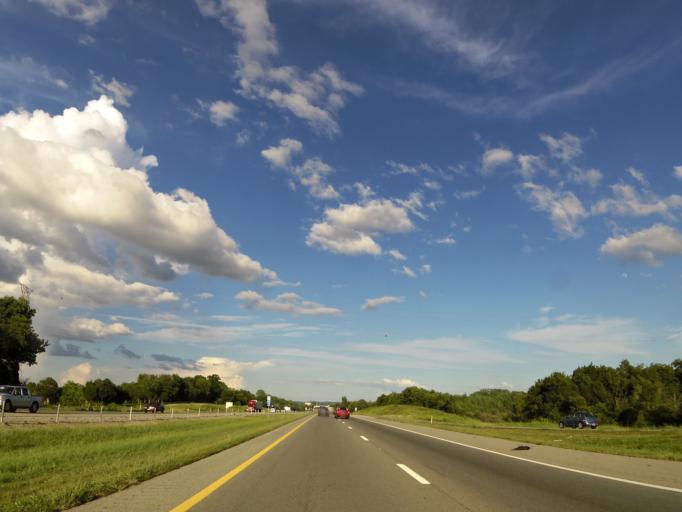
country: US
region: Tennessee
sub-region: Wilson County
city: Lebanon
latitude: 36.1835
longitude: -86.3471
